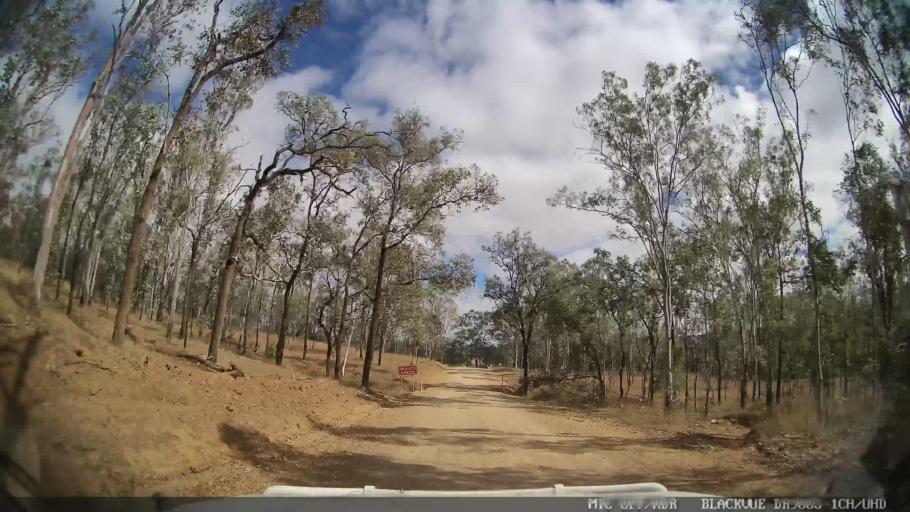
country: AU
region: Queensland
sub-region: Gladstone
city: Toolooa
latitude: -24.6853
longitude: 151.3265
